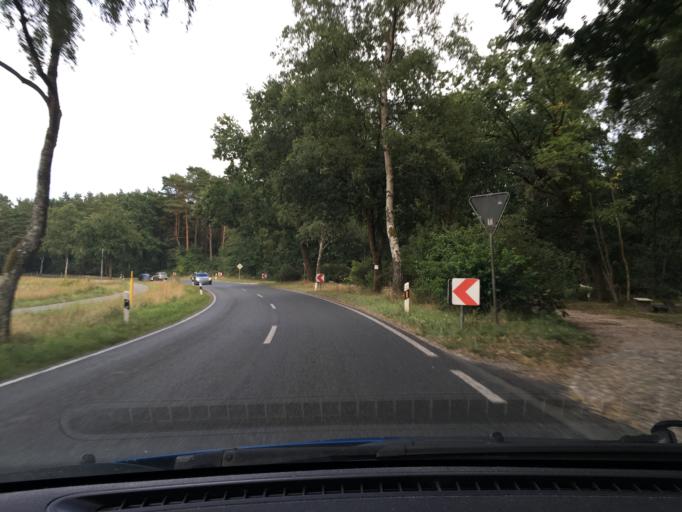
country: DE
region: Lower Saxony
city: Undeloh
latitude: 53.1953
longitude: 10.0116
